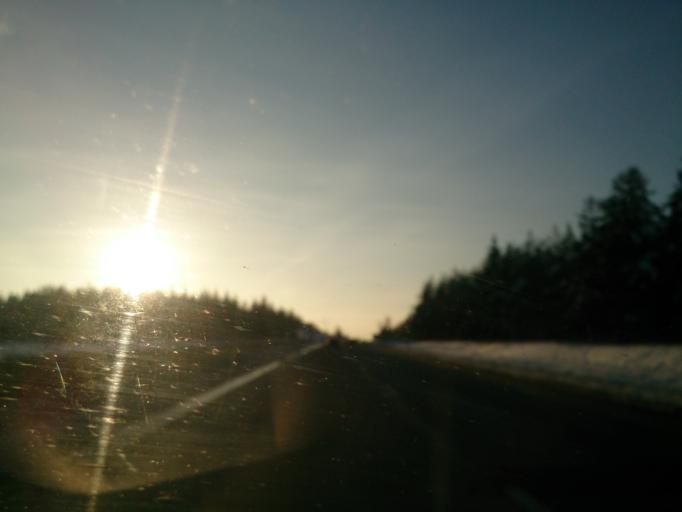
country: SE
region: OEstergoetland
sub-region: Norrkopings Kommun
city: Kimstad
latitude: 58.4927
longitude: 15.9652
